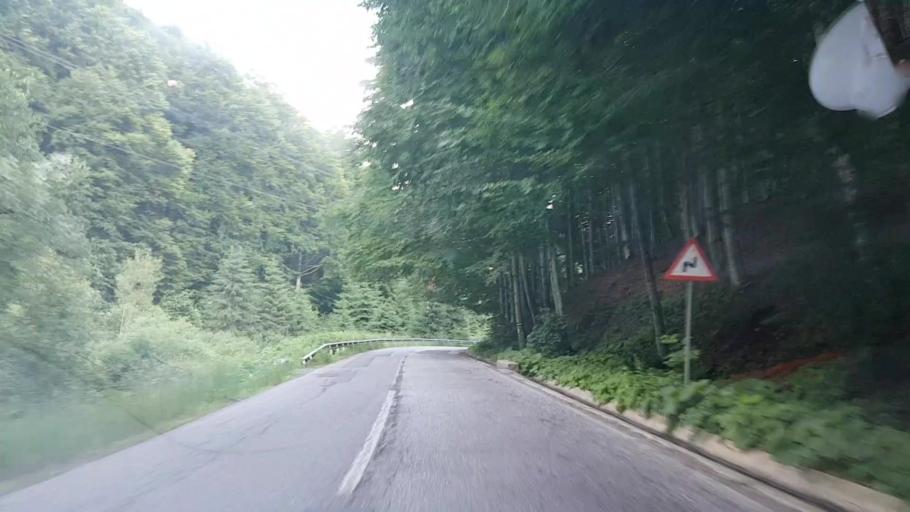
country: RO
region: Harghita
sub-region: Comuna Praid
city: Ocna de Sus
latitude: 46.5959
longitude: 25.2408
